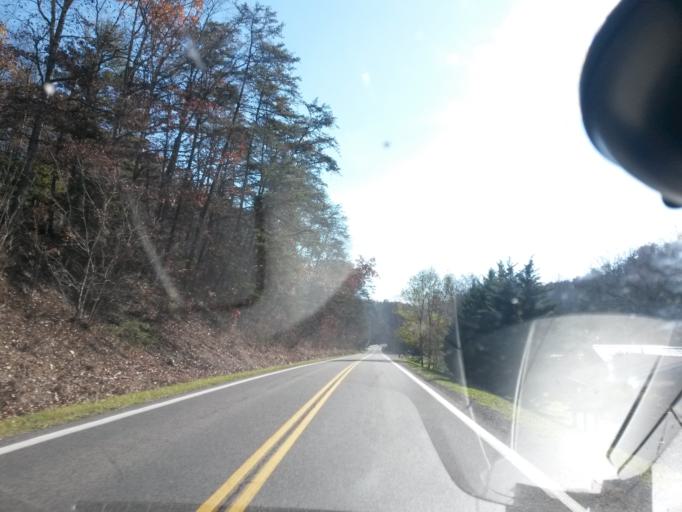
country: US
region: Virginia
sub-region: Alleghany County
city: Clifton Forge
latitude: 37.8260
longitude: -79.7560
